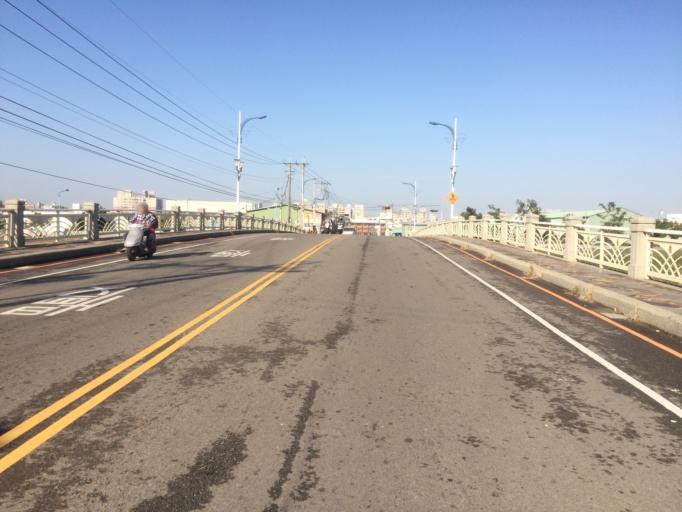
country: TW
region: Taiwan
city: Fengyuan
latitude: 24.2045
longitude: 120.7158
